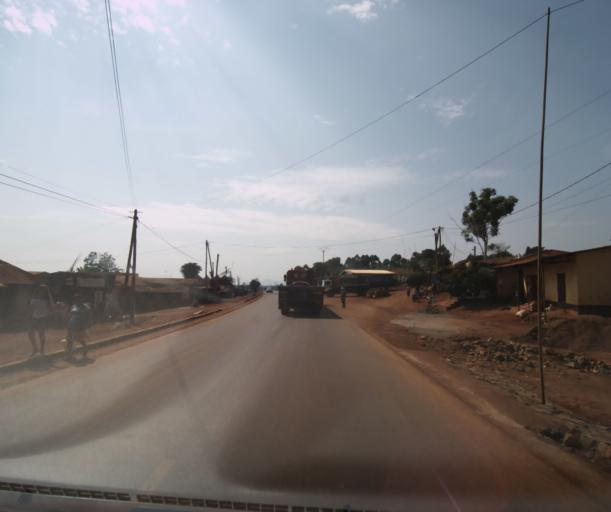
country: CM
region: West
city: Mbouda
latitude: 5.6206
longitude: 10.2683
